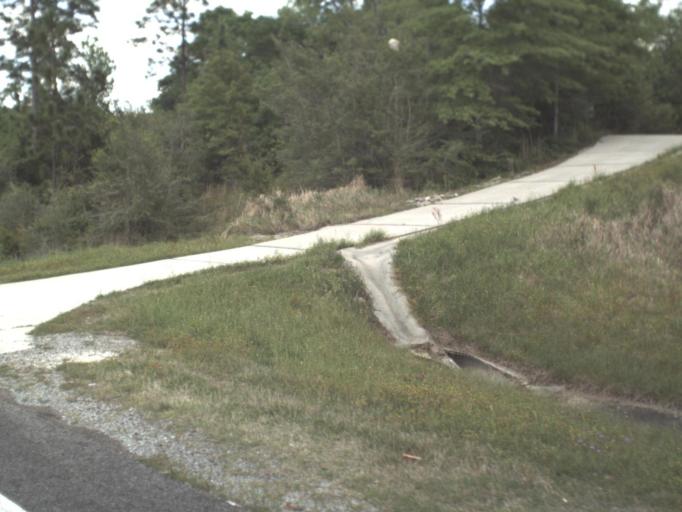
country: US
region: Florida
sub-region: Escambia County
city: Molino
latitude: 30.7680
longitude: -87.3405
